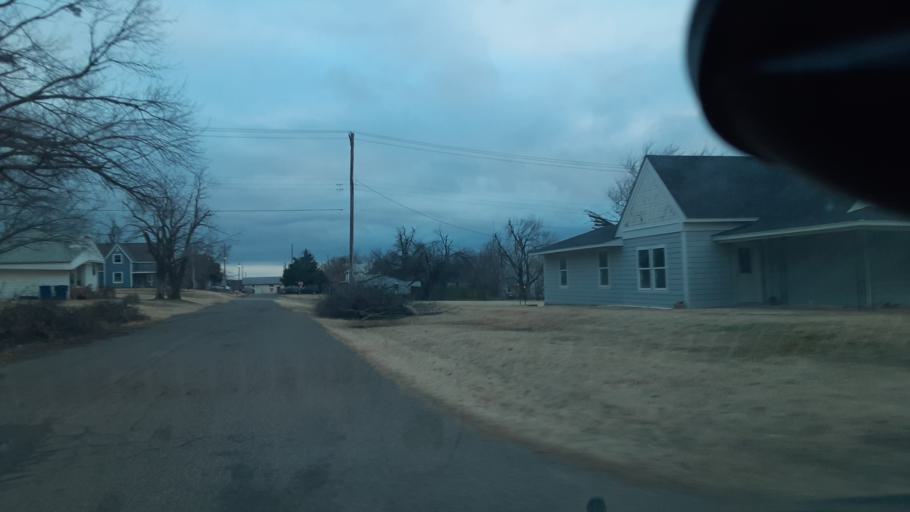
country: US
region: Oklahoma
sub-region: Logan County
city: Guthrie
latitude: 35.8760
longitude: -97.4137
